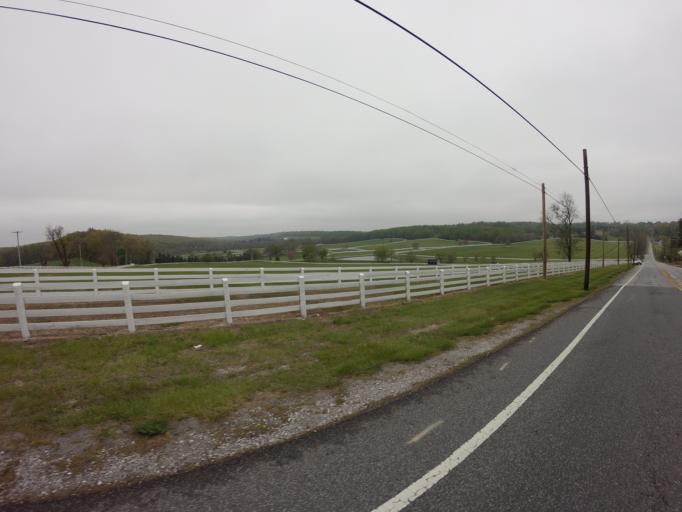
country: US
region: Maryland
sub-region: Baltimore County
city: Hunt Valley
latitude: 39.5700
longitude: -76.6583
